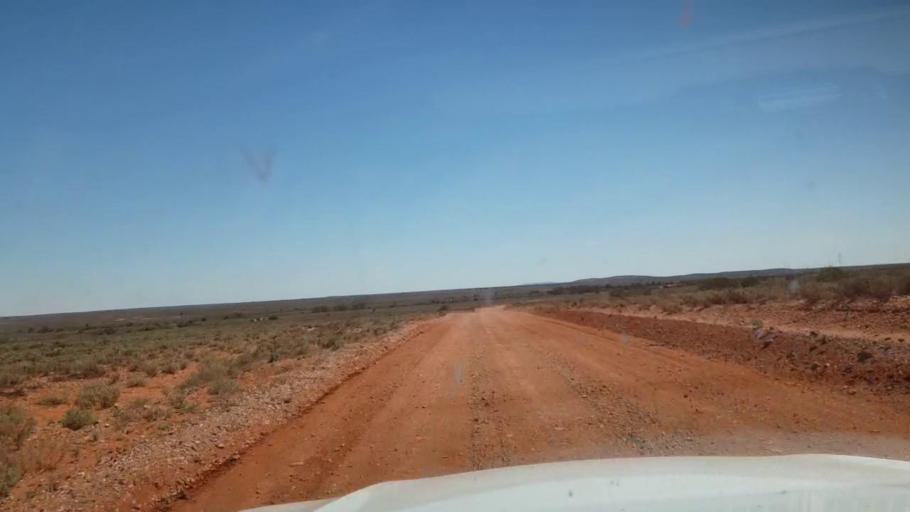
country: AU
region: South Australia
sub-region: Whyalla
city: Whyalla
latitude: -32.6857
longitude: 137.1188
